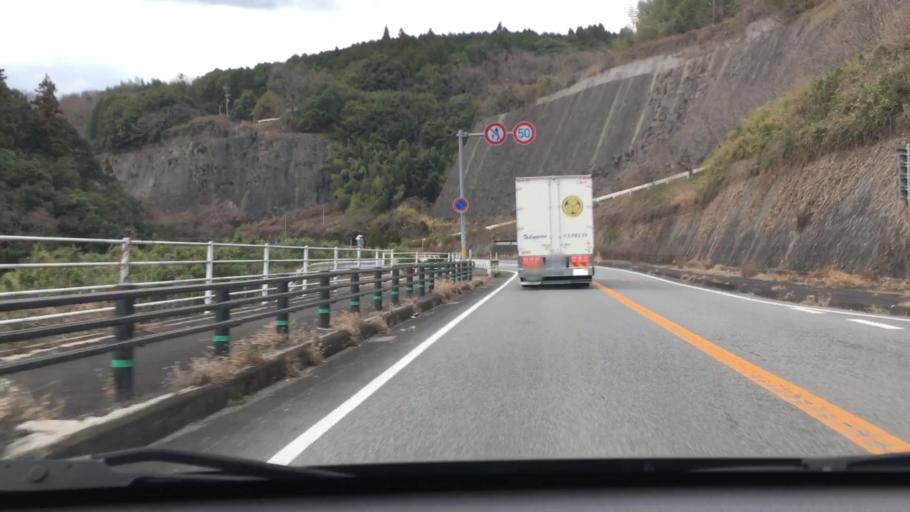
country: JP
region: Oita
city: Usuki
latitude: 33.0680
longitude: 131.6552
